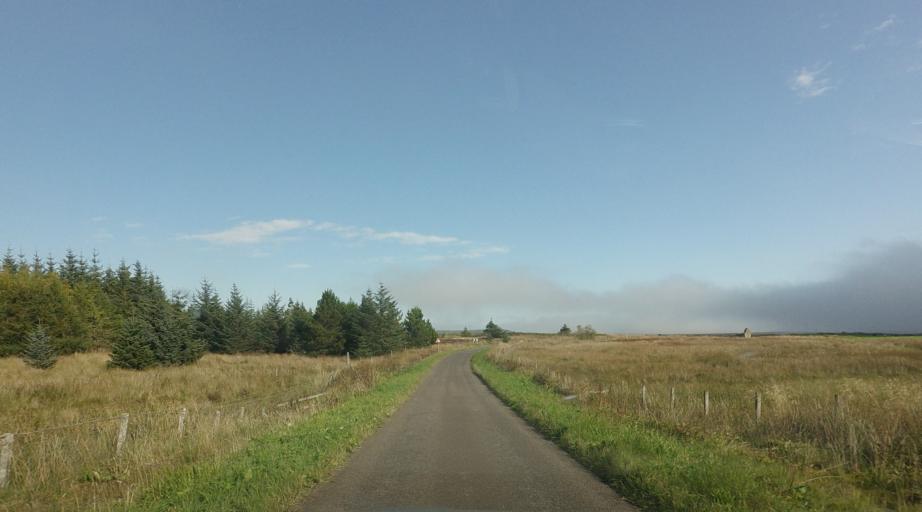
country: GB
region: Scotland
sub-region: Highland
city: Wick
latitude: 58.3357
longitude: -3.3416
